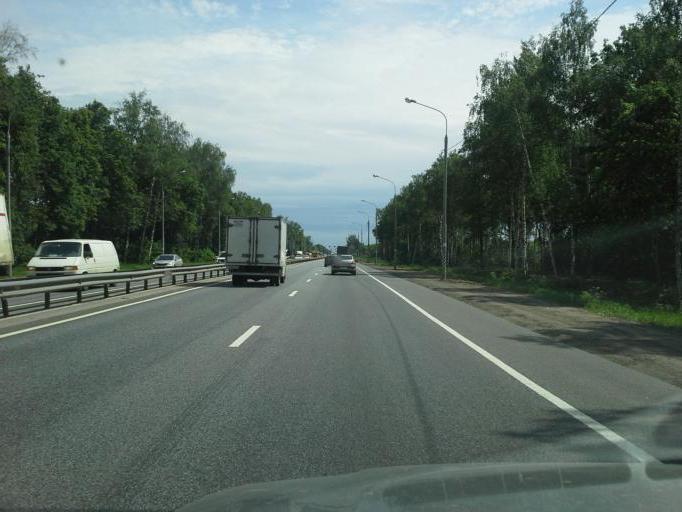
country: RU
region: Moskovskaya
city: Staraya Kupavna
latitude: 55.8178
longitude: 38.1511
